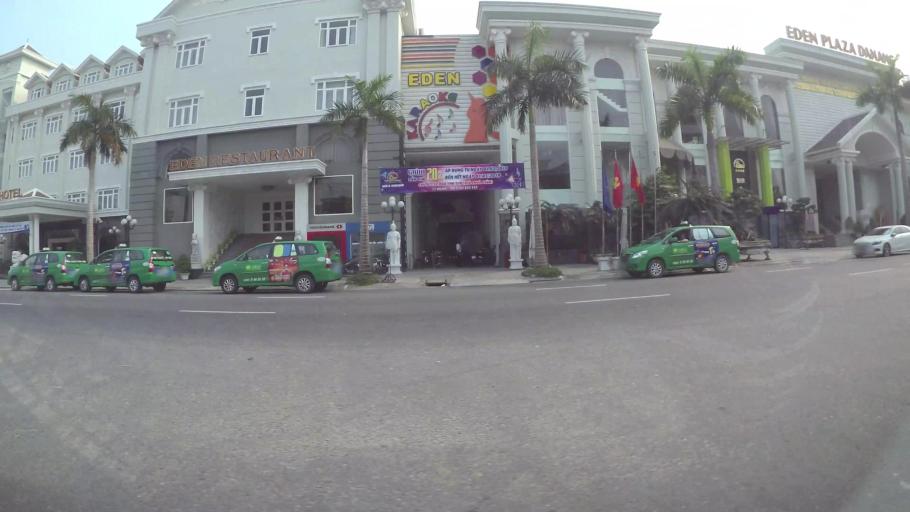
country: VN
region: Da Nang
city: Da Nang
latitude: 16.0486
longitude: 108.2162
